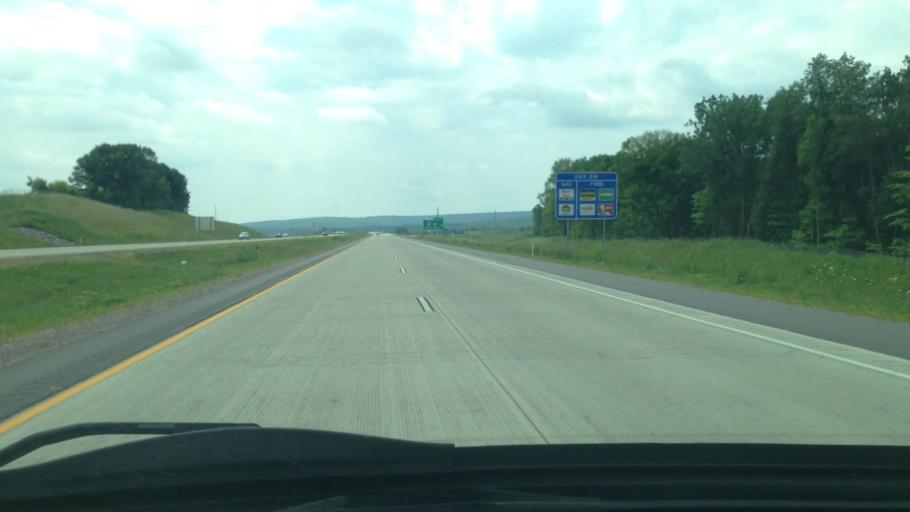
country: US
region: Wisconsin
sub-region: Sauk County
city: West Baraboo
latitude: 43.4676
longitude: -89.7770
